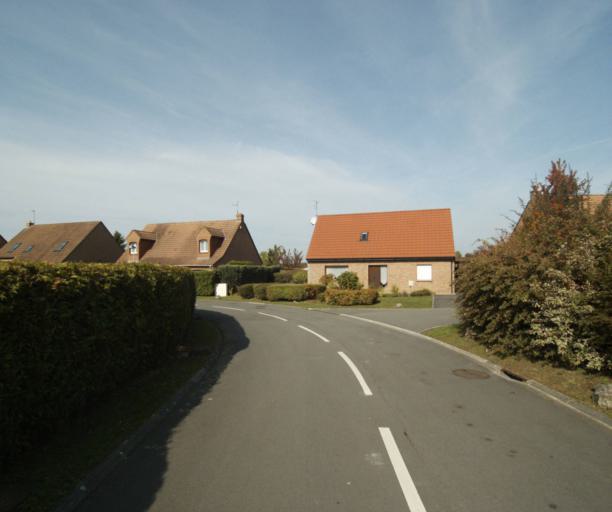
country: FR
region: Nord-Pas-de-Calais
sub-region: Departement du Nord
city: Capinghem
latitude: 50.6486
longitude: 2.9583
